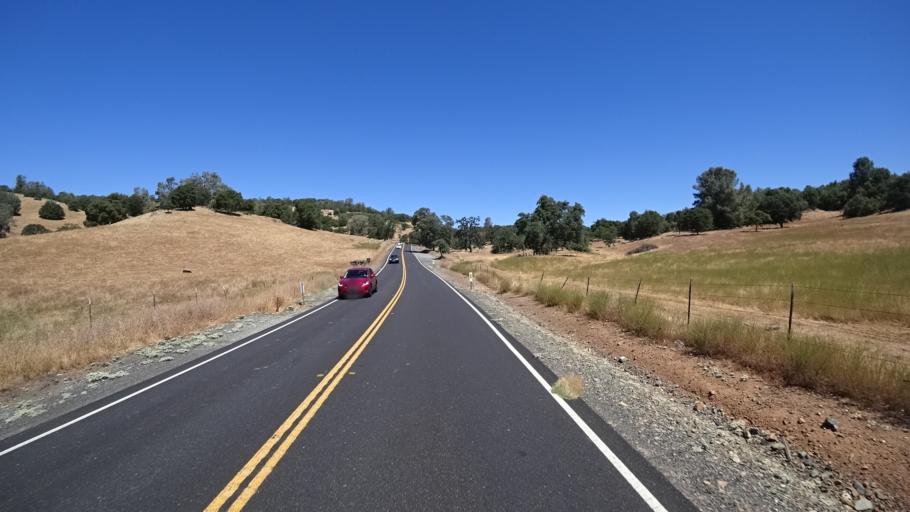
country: US
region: California
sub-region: Calaveras County
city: Copperopolis
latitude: 38.0321
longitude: -120.6481
